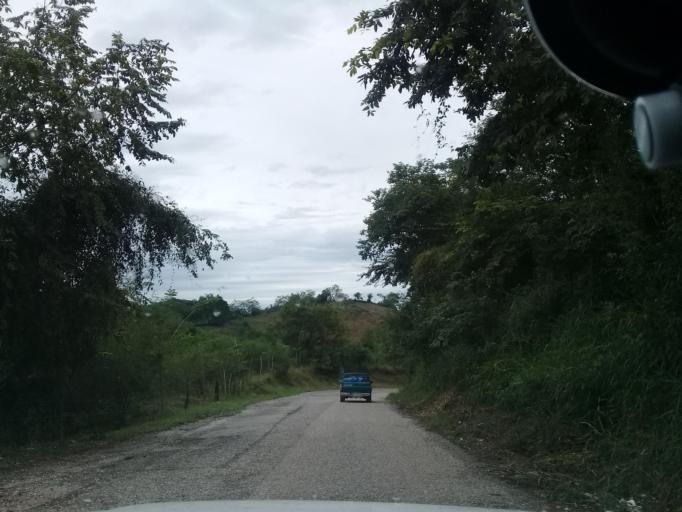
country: MX
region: Veracruz
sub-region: Chalma
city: San Pedro Coyutla
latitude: 21.2145
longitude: -98.3777
